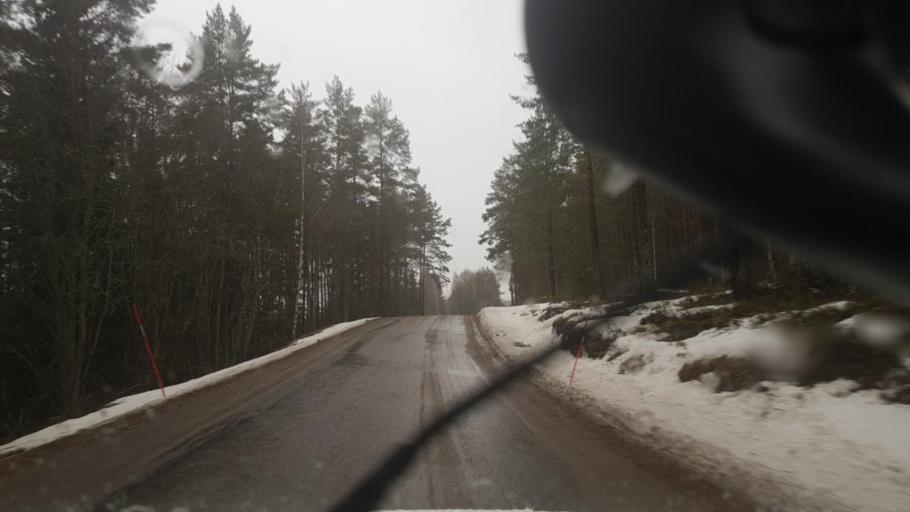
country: SE
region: Vaermland
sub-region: Eda Kommun
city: Amotfors
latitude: 59.8152
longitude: 12.3608
